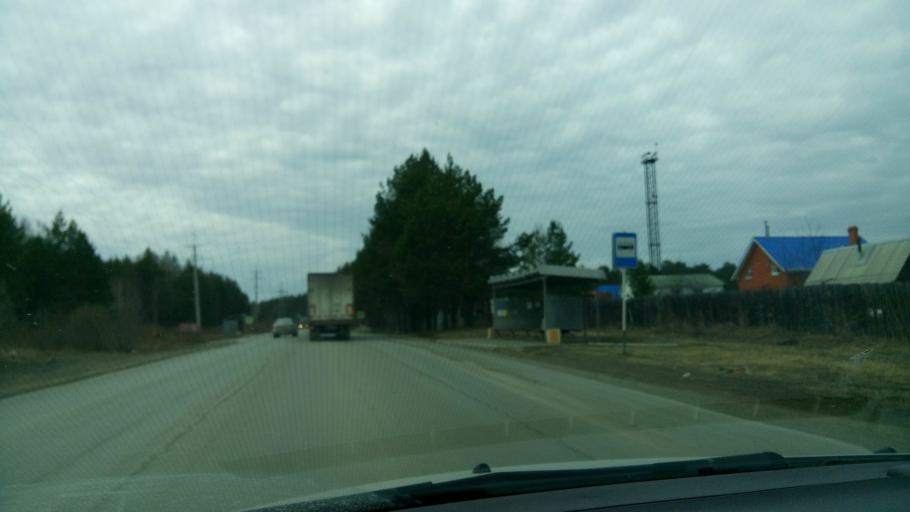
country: RU
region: Sverdlovsk
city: Verkhnyaya Pyshma
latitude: 56.9556
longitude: 60.6535
